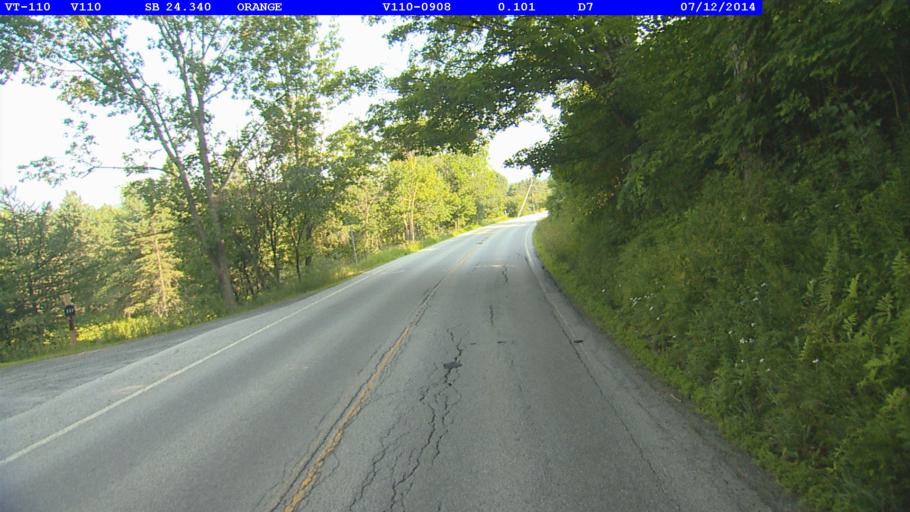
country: US
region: Vermont
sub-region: Washington County
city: South Barre
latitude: 44.1256
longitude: -72.4297
